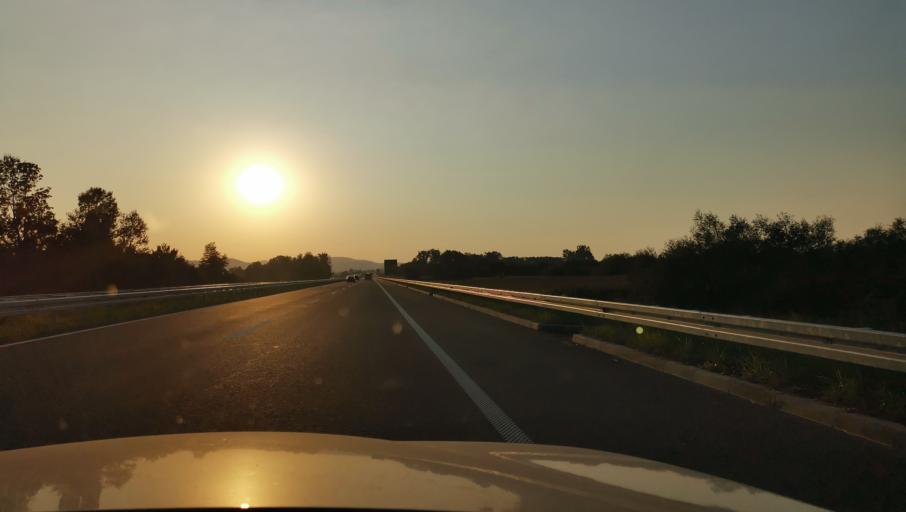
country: RS
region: Central Serbia
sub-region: Kolubarski Okrug
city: Lajkovac
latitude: 44.3525
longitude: 20.1491
